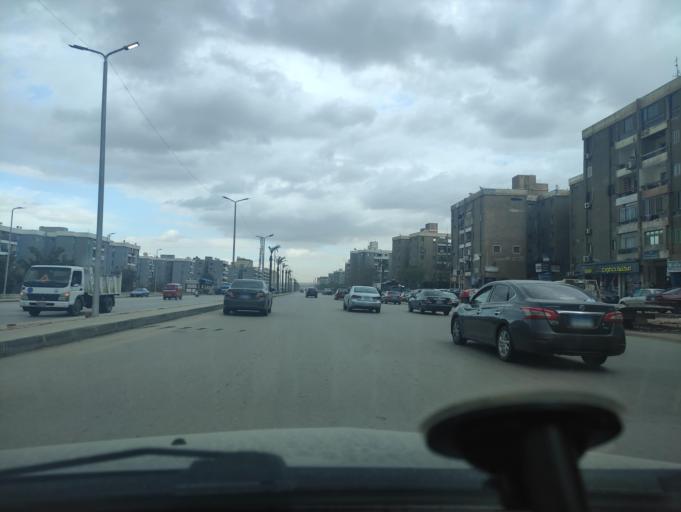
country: EG
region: Muhafazat al Qahirah
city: Cairo
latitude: 30.0498
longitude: 31.3870
